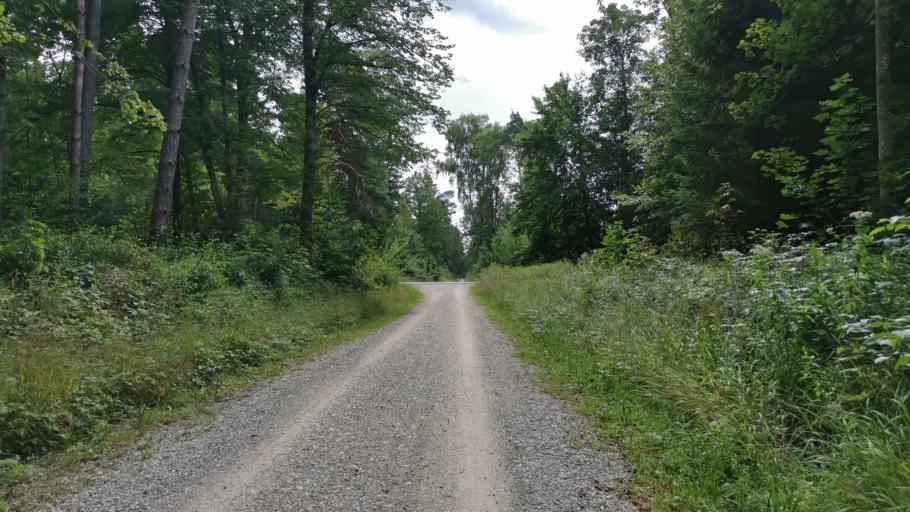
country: DE
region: Bavaria
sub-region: Upper Bavaria
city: Unterhaching
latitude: 48.0804
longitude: 11.5732
